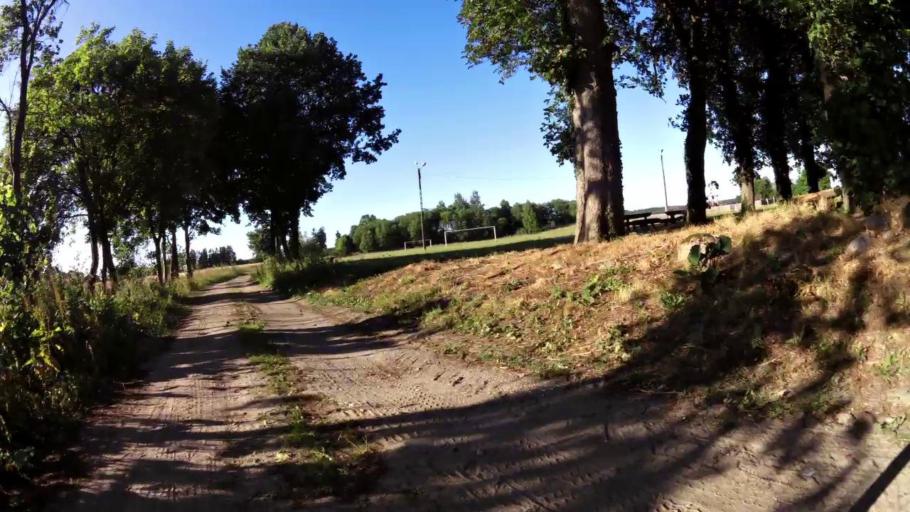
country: PL
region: West Pomeranian Voivodeship
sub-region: Powiat swidwinski
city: Swidwin
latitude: 53.7008
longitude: 15.8234
